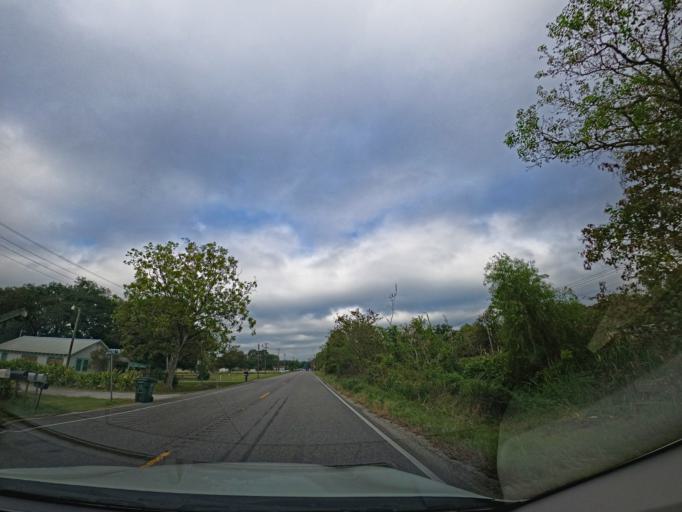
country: US
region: Louisiana
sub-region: Saint Mary Parish
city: Amelia
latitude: 29.6394
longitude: -90.9555
